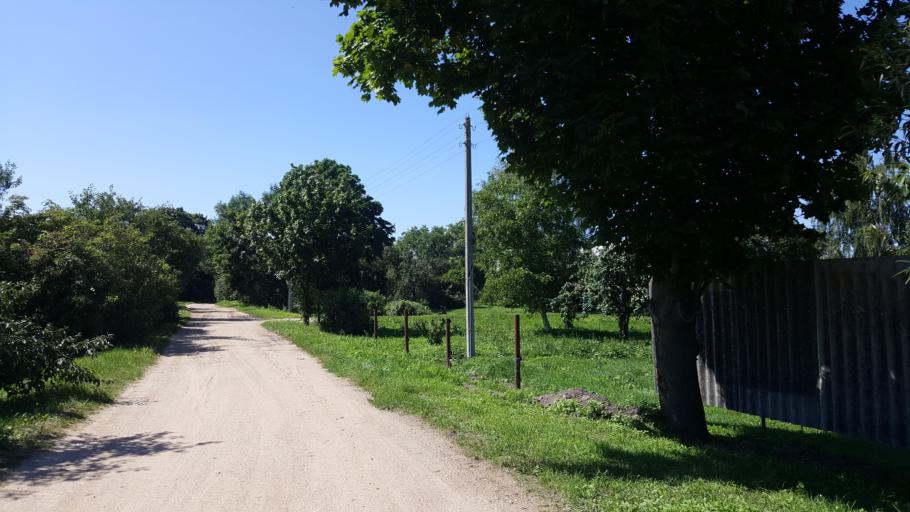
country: BY
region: Brest
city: Charnawchytsy
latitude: 52.2103
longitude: 23.7903
